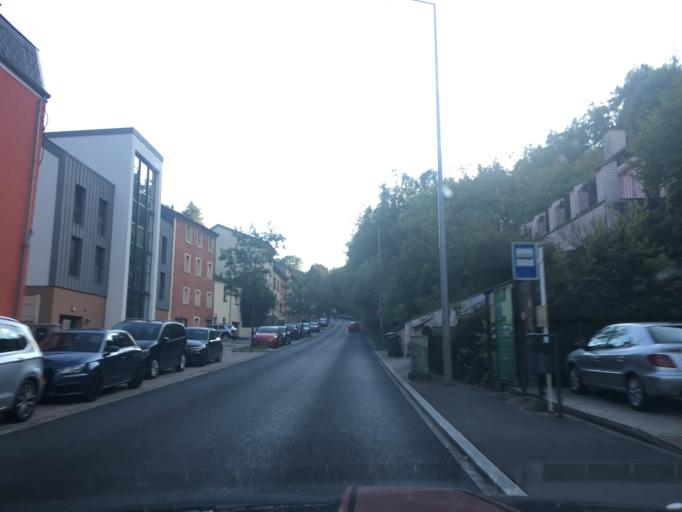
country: LU
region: Luxembourg
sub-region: Canton d'Esch-sur-Alzette
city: Differdange
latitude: 49.5176
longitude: 5.8800
